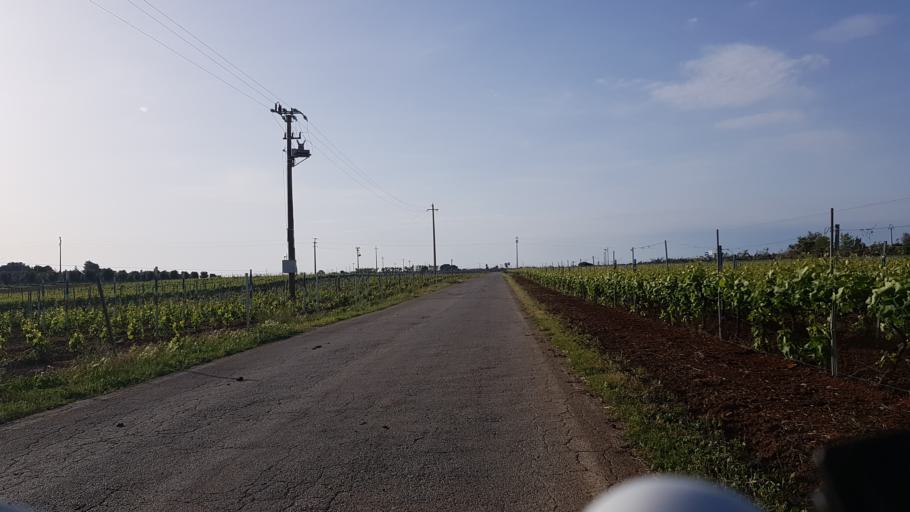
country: IT
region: Apulia
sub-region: Provincia di Brindisi
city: Mesagne
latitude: 40.5862
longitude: 17.8578
